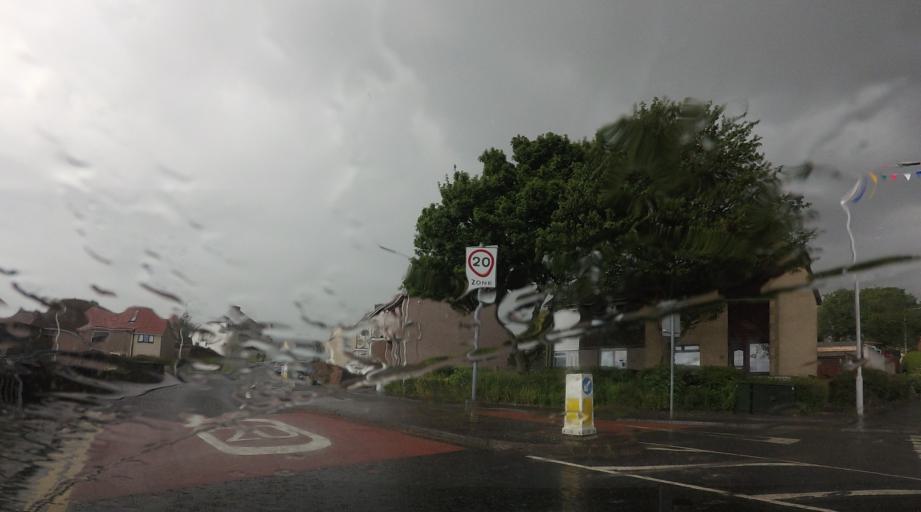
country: GB
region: Scotland
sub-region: Fife
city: Ballingry
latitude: 56.1576
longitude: -3.3220
